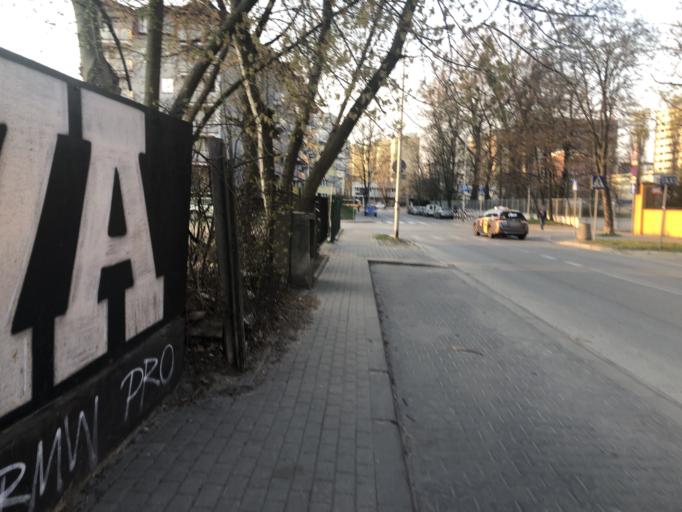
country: PL
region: Masovian Voivodeship
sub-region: Warszawa
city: Ochota
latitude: 52.2271
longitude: 20.9689
